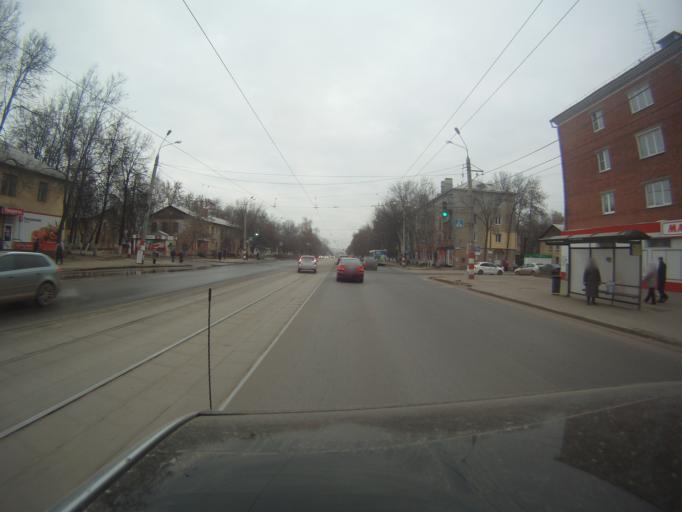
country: RU
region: Nizjnij Novgorod
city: Nizhniy Novgorod
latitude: 56.2941
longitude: 44.0212
